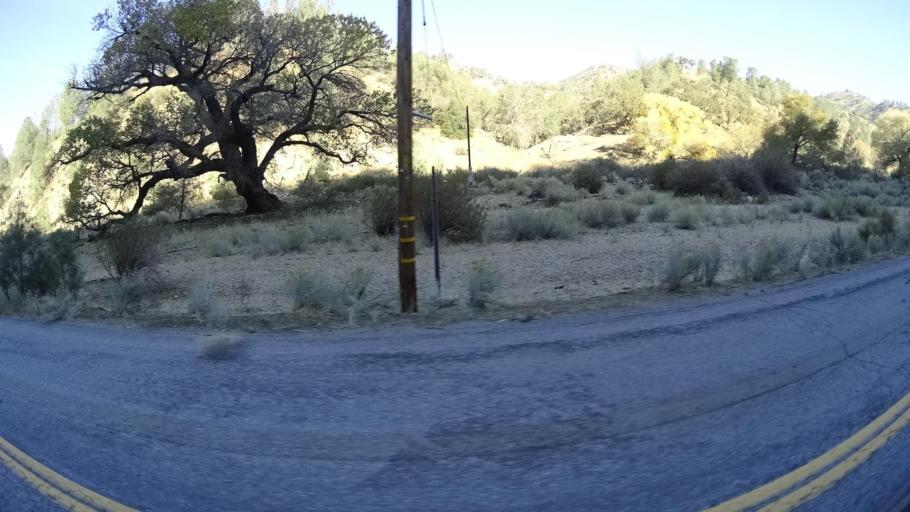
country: US
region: California
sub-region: Kern County
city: Golden Hills
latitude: 35.3041
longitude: -118.4477
